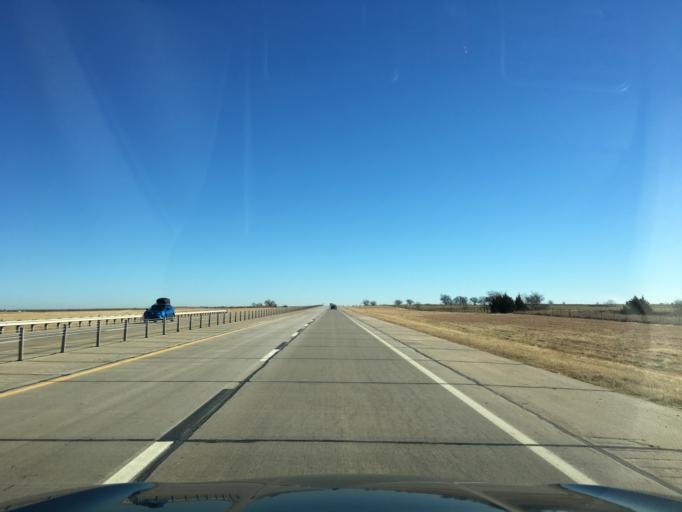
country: US
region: Oklahoma
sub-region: Noble County
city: Perry
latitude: 36.4011
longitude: -97.2463
